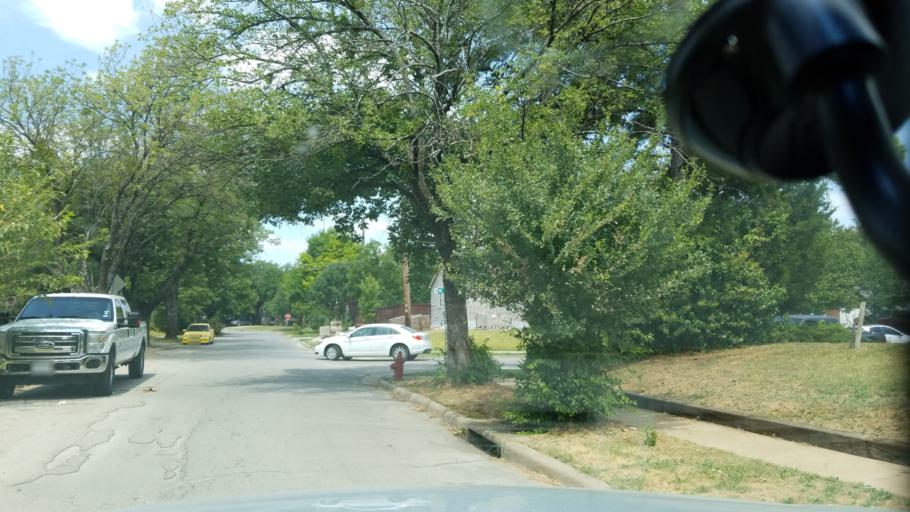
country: US
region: Texas
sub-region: Dallas County
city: Grand Prairie
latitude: 32.7533
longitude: -96.9767
